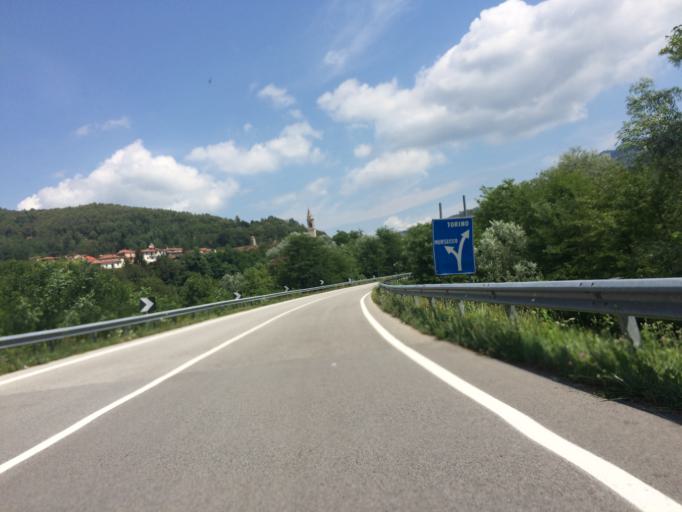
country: IT
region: Piedmont
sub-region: Provincia di Cuneo
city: Priola
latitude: 44.2376
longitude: 8.0154
